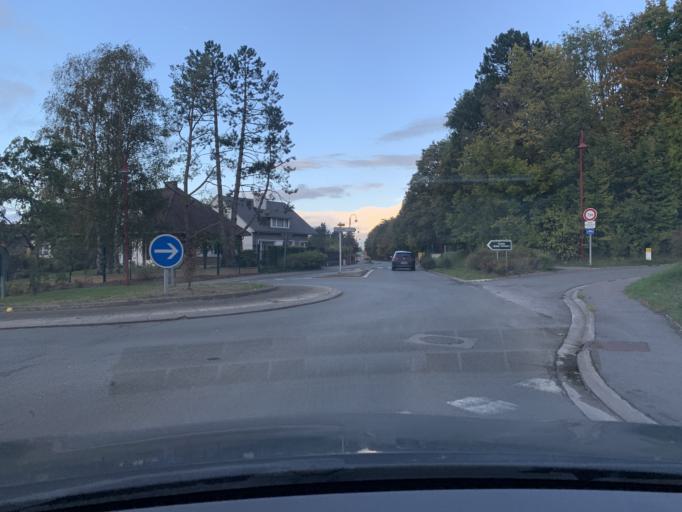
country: FR
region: Nord-Pas-de-Calais
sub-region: Departement du Nord
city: Proville
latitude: 50.1592
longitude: 3.2107
